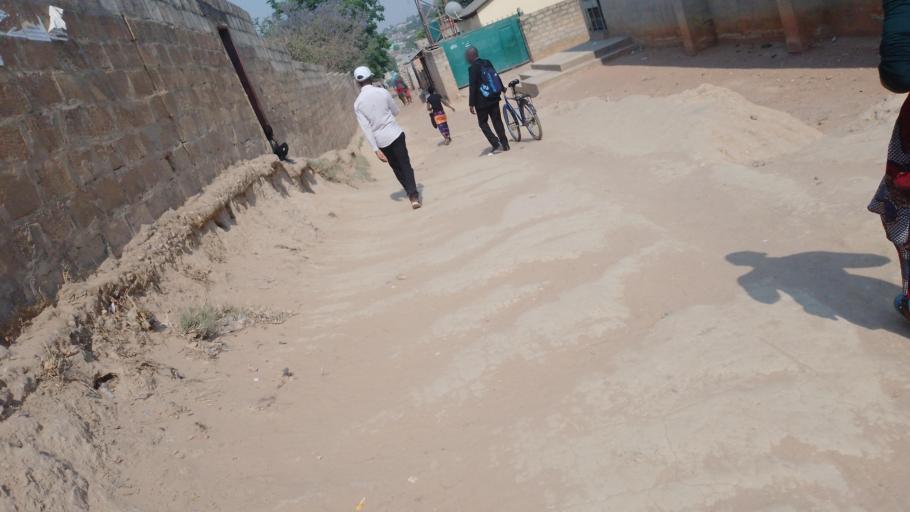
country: ZM
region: Lusaka
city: Lusaka
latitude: -15.4022
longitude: 28.3670
